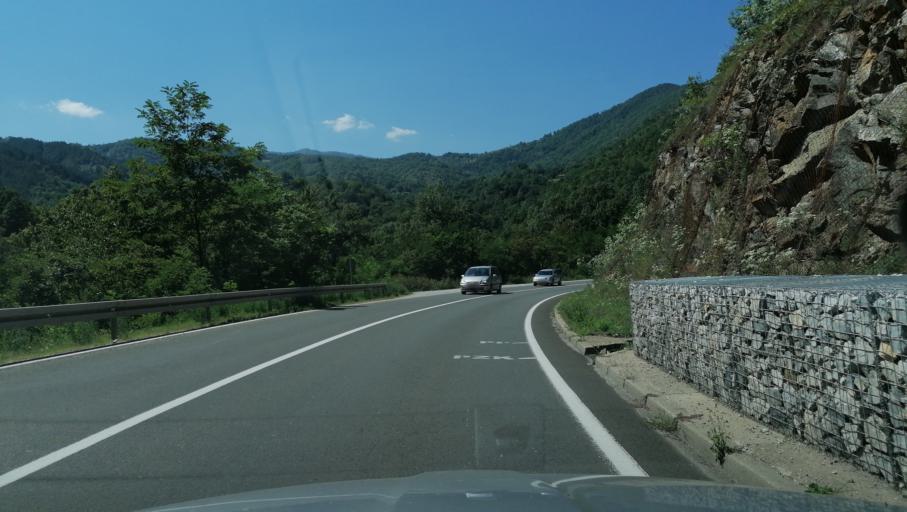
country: RS
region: Central Serbia
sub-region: Raski Okrug
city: Kraljevo
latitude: 43.6157
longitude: 20.5515
